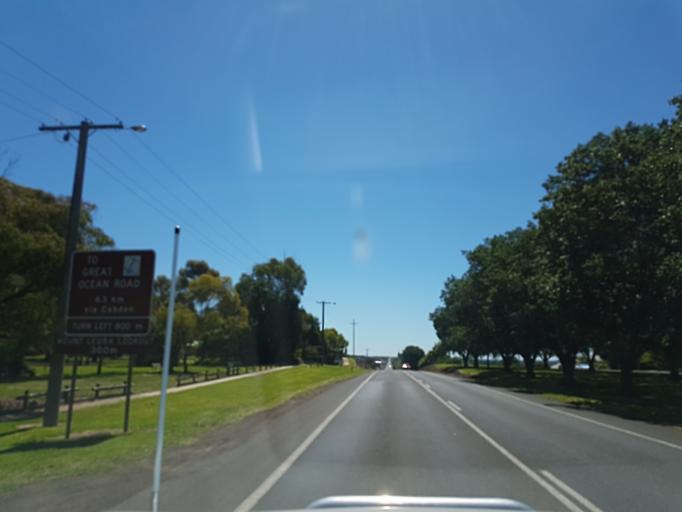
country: AU
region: Victoria
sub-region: Colac-Otway
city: Colac
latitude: -38.2383
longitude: 143.1561
